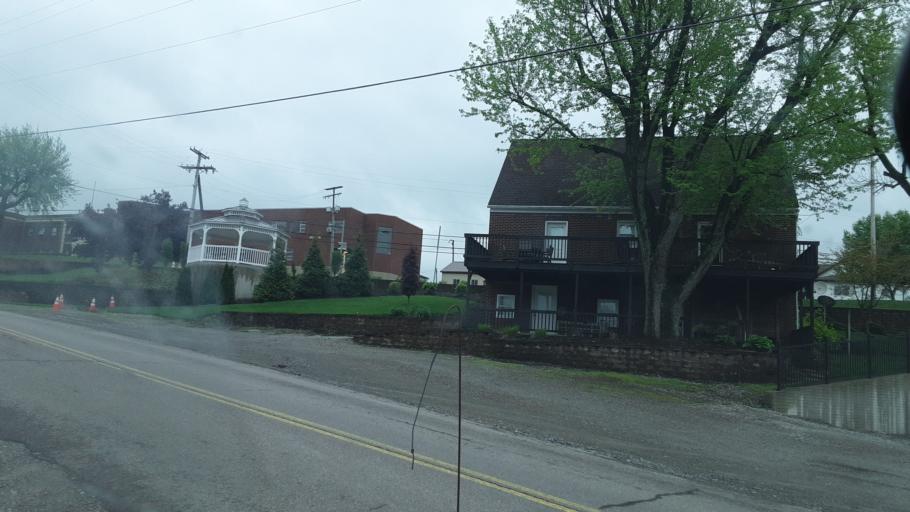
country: US
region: Ohio
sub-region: Holmes County
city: Millersburg
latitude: 40.5621
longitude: -81.8025
